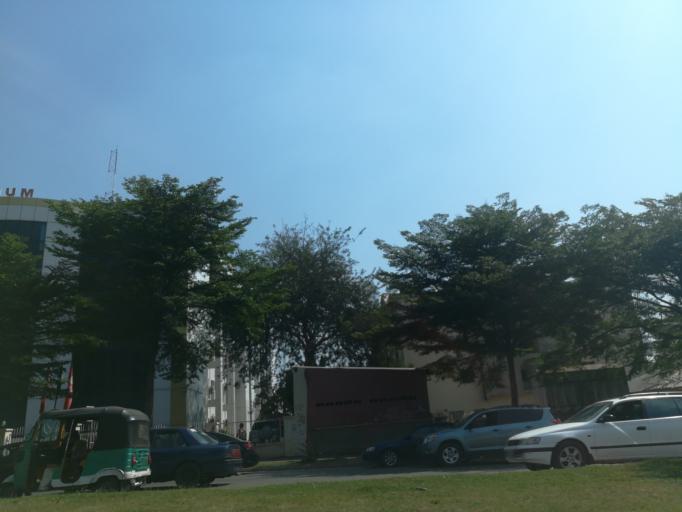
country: NG
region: Abuja Federal Capital Territory
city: Abuja
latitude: 9.0675
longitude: 7.4391
